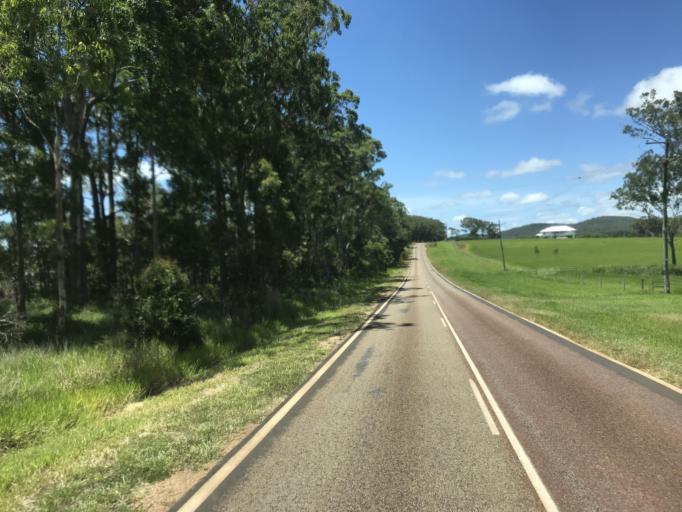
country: AU
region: Queensland
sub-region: Tablelands
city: Ravenshoe
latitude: -17.5183
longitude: 145.4514
